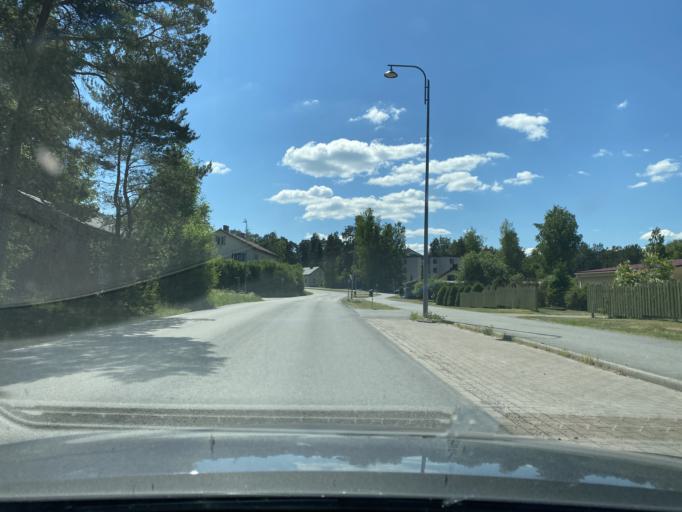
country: FI
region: Satakunta
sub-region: Rauma
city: Eura
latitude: 61.1225
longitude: 22.1597
